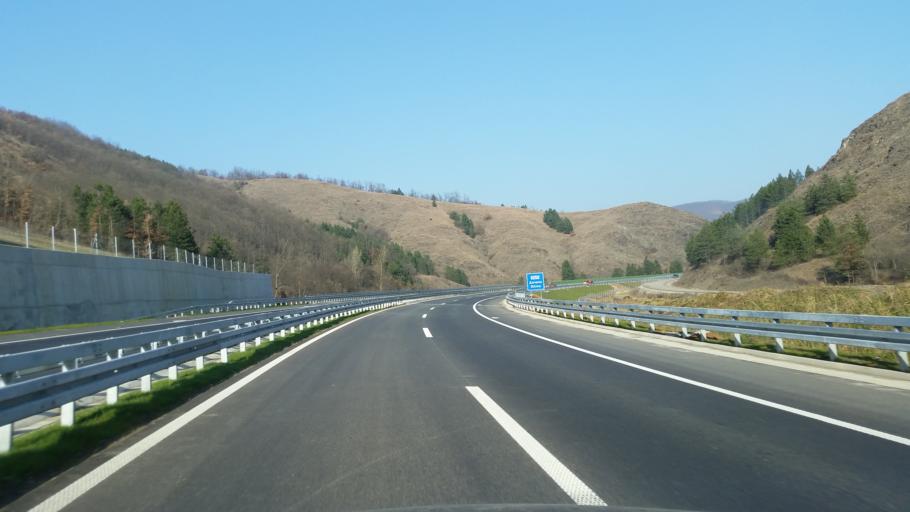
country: RS
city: Prislonica
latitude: 43.9898
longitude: 20.3996
